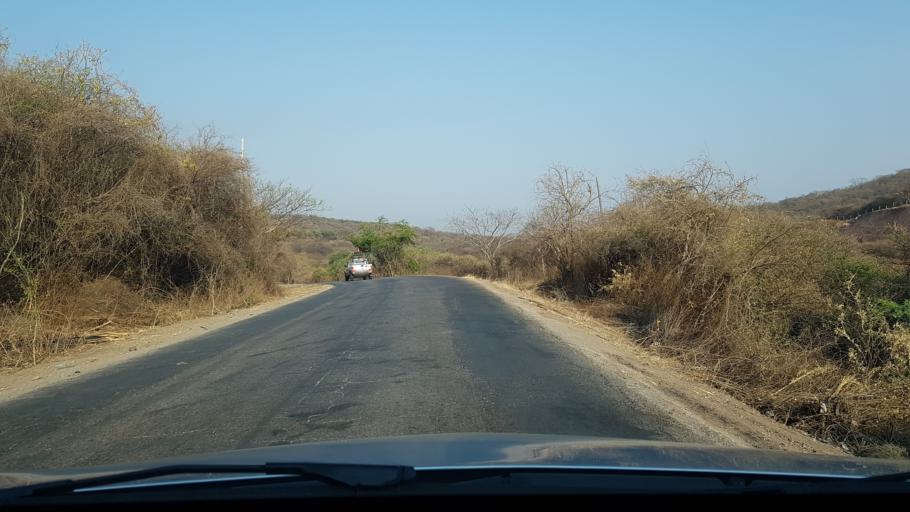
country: MX
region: Morelos
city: Tlaltizapan
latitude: 18.6759
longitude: -99.0719
